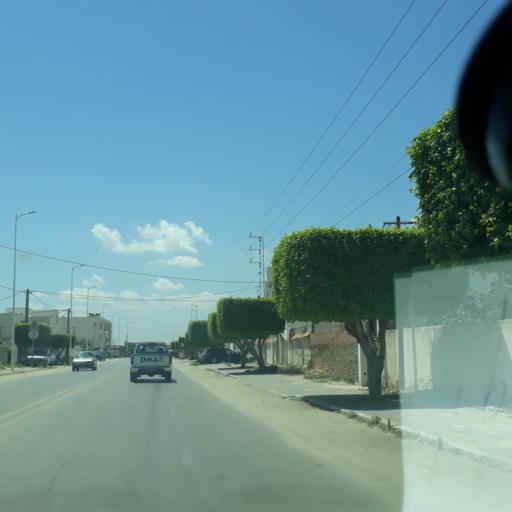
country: TN
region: Safaqis
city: Al Qarmadah
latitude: 34.8167
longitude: 10.7437
